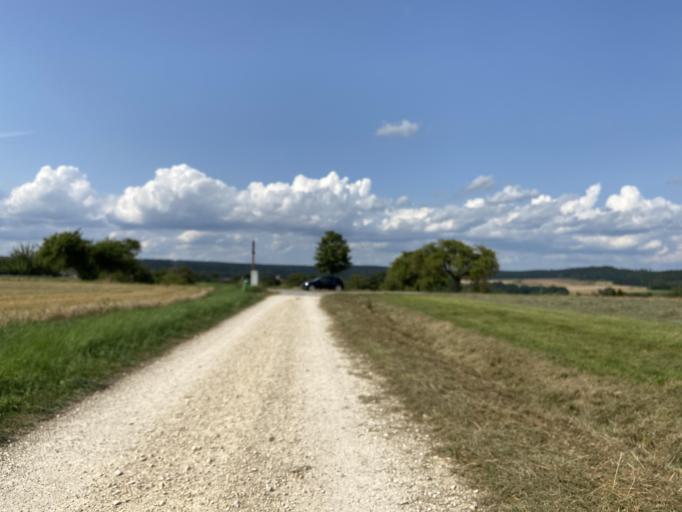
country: DE
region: Baden-Wuerttemberg
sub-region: Tuebingen Region
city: Bingen
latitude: 48.1014
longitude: 9.2780
